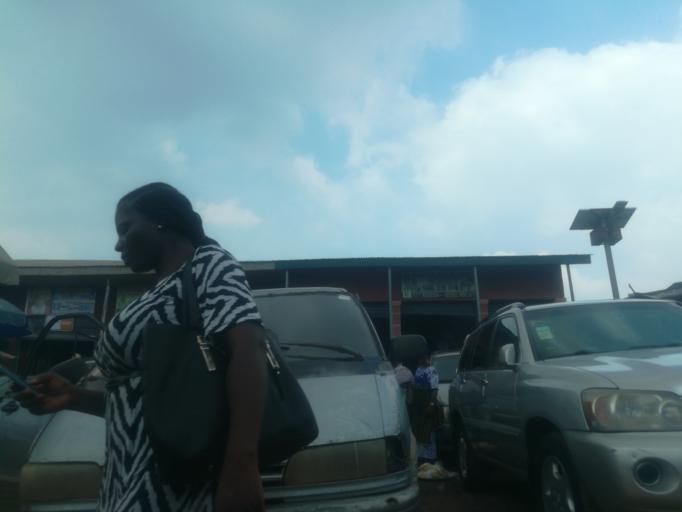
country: NG
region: Oyo
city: Ibadan
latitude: 7.3923
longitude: 3.9576
